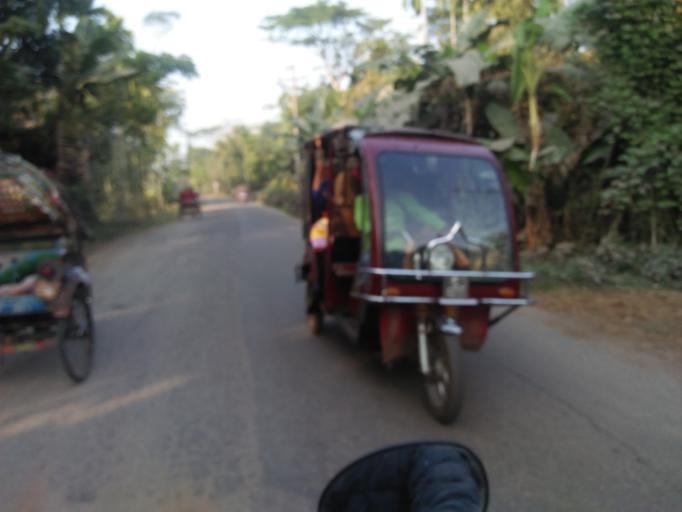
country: BD
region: Barisal
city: Bhola
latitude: 22.7443
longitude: 90.6344
